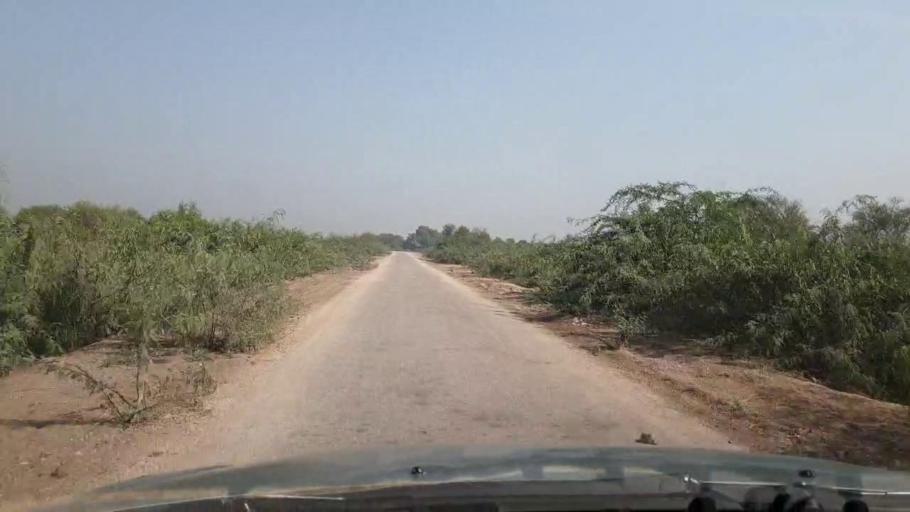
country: PK
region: Sindh
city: Tando Jam
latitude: 25.3075
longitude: 68.5384
